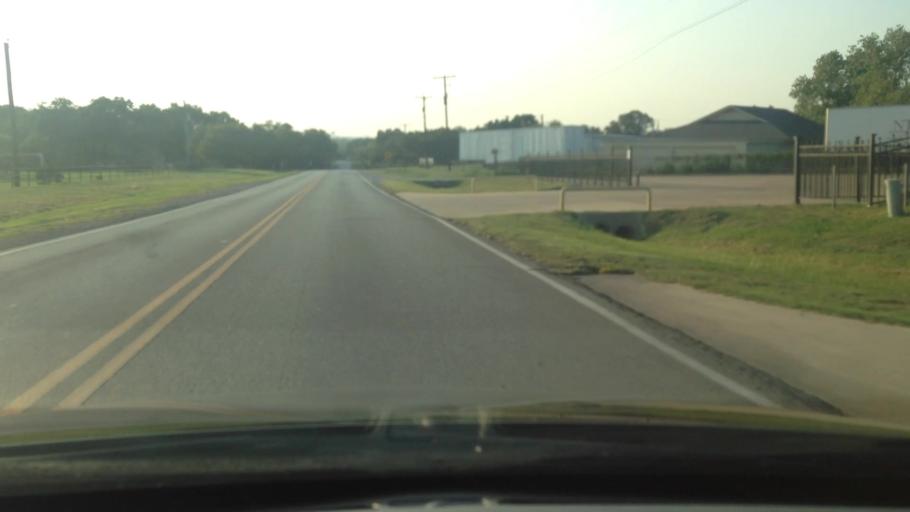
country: US
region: Texas
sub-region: Tarrant County
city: Rendon
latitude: 32.5936
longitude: -97.2549
